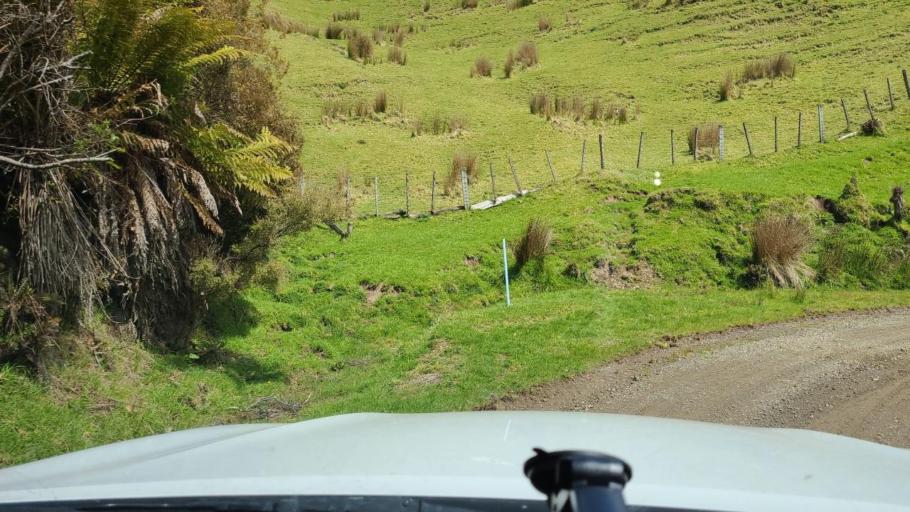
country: NZ
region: Bay of Plenty
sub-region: Opotiki District
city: Opotiki
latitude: -38.2271
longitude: 177.5854
